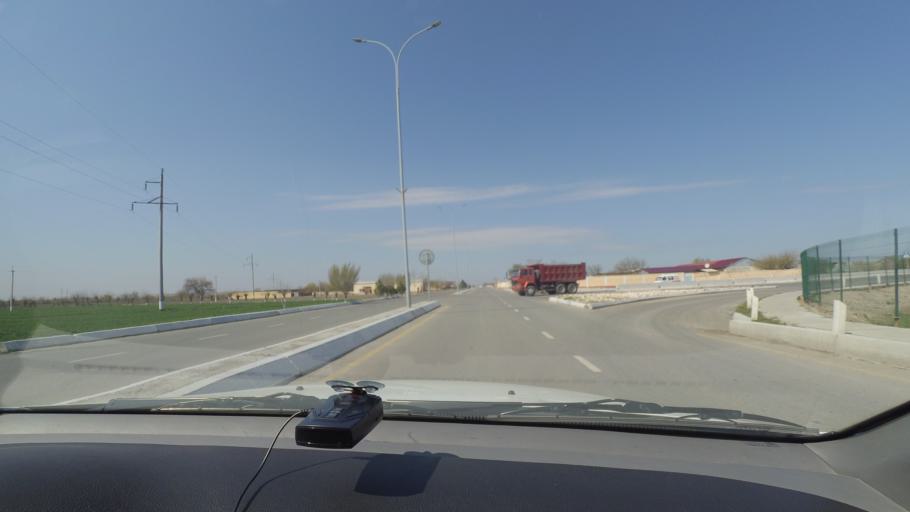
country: UZ
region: Bukhara
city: Galaosiyo
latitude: 39.8035
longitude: 64.5124
